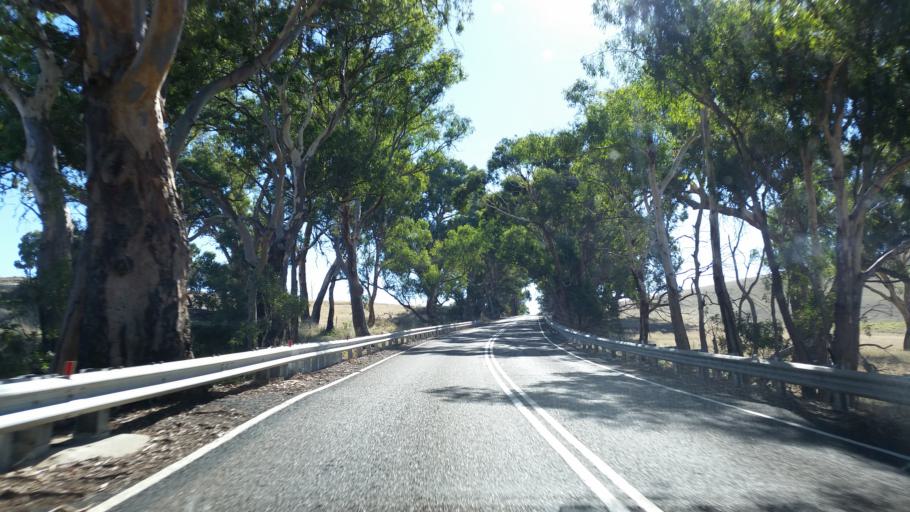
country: AU
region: South Australia
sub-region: Adelaide Hills
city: Birdwood
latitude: -34.8164
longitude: 139.0463
